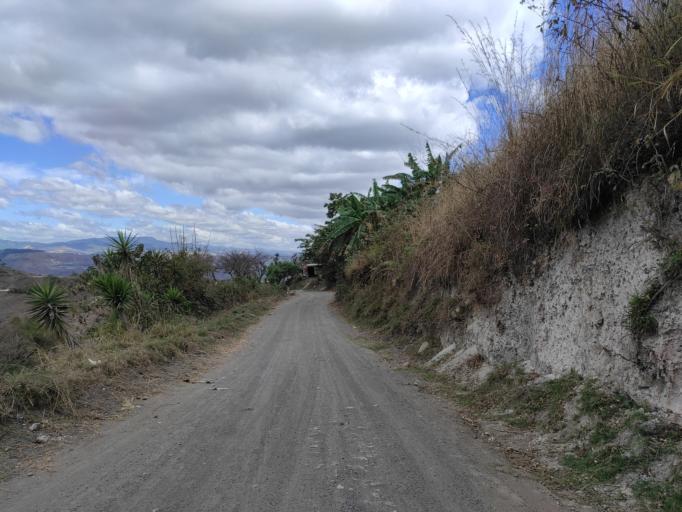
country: GT
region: Guatemala
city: Villa Canales
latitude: 14.4430
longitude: -90.5716
